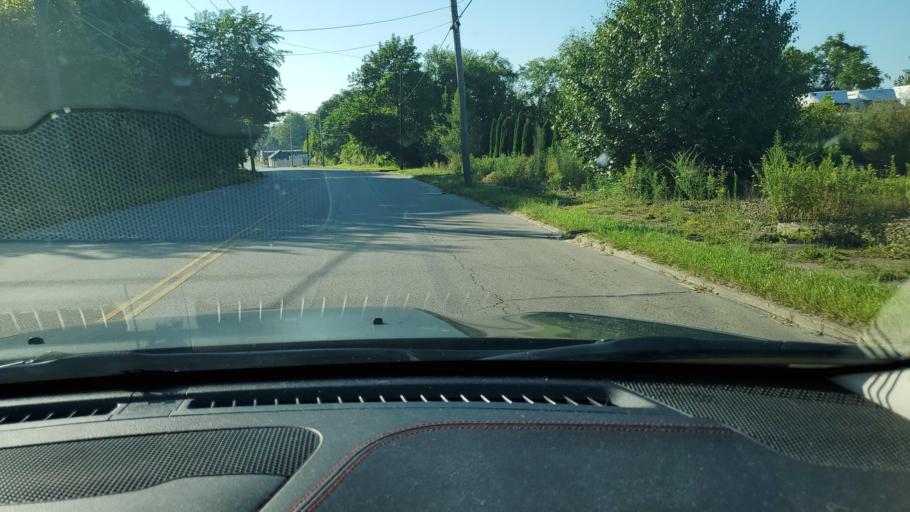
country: US
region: Ohio
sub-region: Mahoning County
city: Campbell
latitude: 41.0872
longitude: -80.6239
